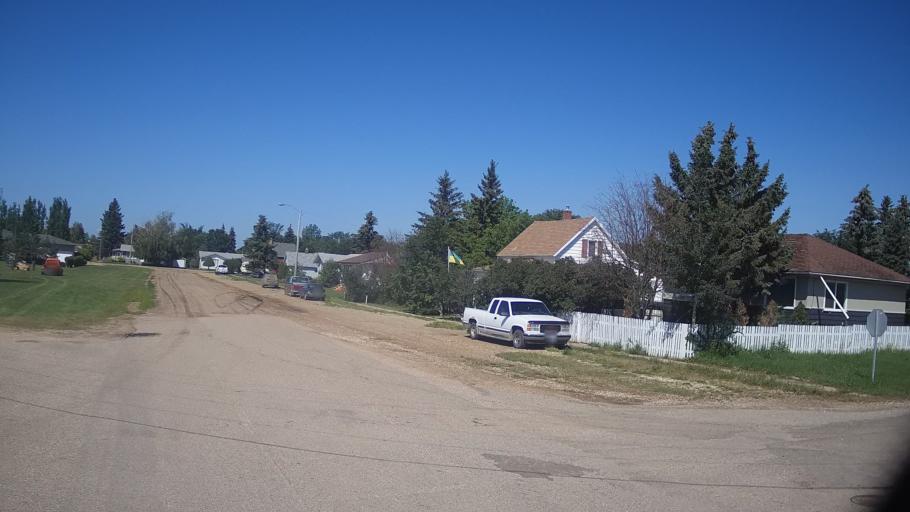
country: CA
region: Saskatchewan
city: Saskatoon
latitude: 51.8966
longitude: -106.0540
